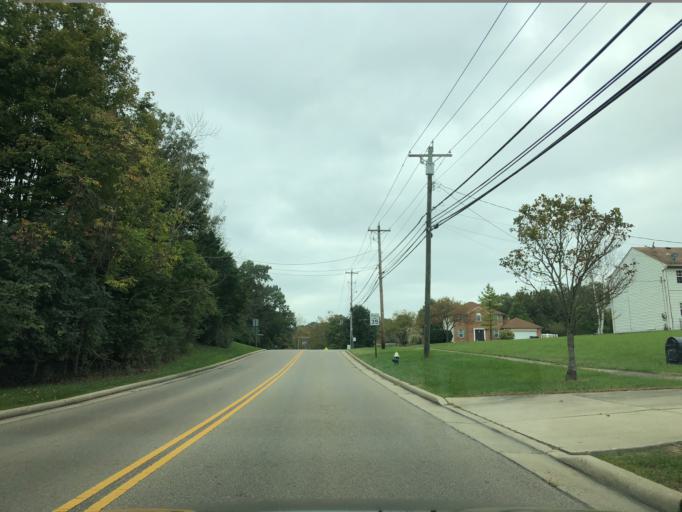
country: US
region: Ohio
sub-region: Hamilton County
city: The Village of Indian Hill
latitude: 39.2678
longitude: -84.2958
